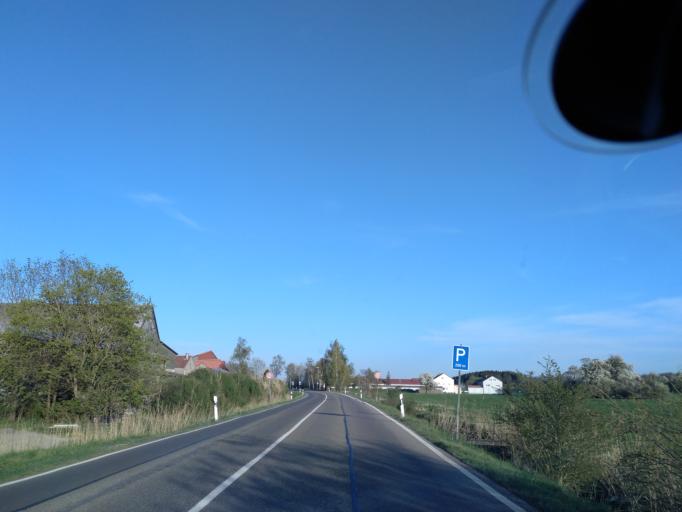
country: DE
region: Baden-Wuerttemberg
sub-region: Regierungsbezirk Stuttgart
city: Kirchberg an der Jagst
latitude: 49.1418
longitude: 9.9938
